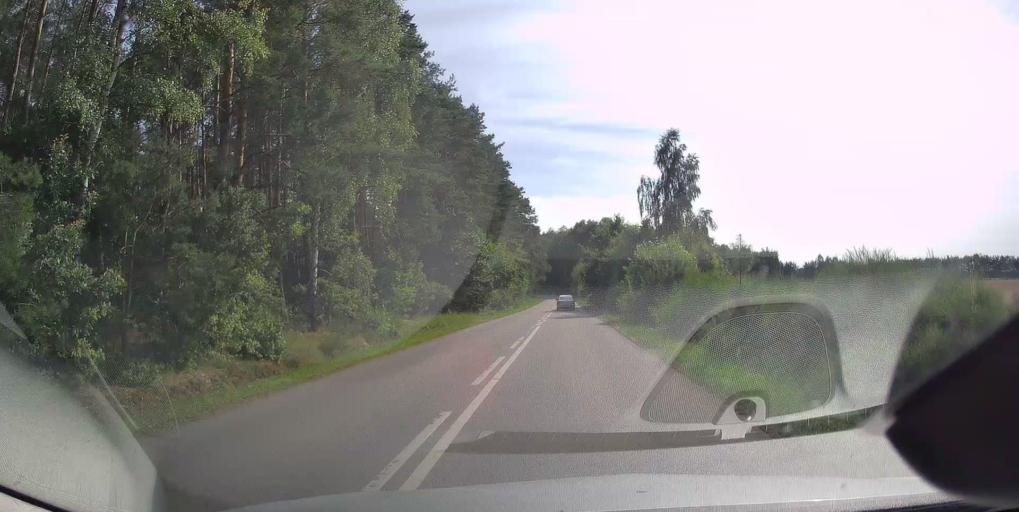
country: PL
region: Lodz Voivodeship
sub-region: Powiat opoczynski
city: Mniszkow
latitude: 51.4029
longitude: 20.0401
